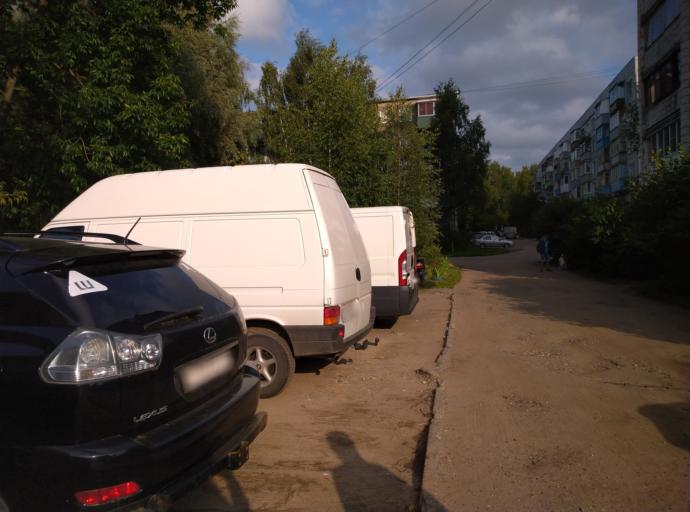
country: RU
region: Kostroma
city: Oktyabr'skiy
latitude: 57.7625
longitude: 40.9688
